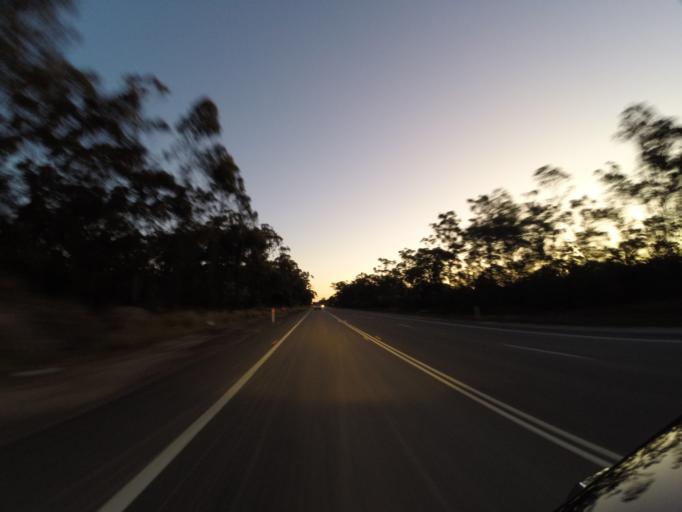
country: AU
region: New South Wales
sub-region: Liverpool
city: Holsworthy
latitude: -34.0241
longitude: 150.9709
